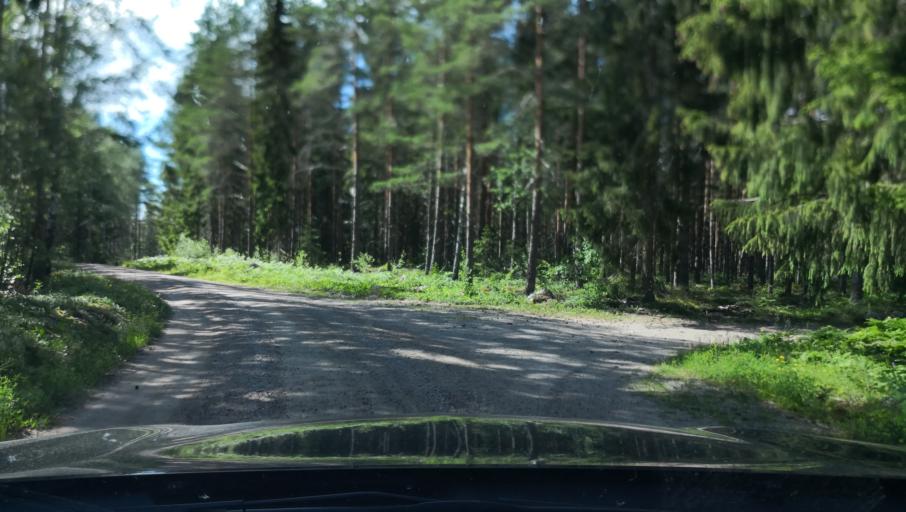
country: SE
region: Vaestmanland
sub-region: Kungsors Kommun
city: Kungsoer
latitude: 59.3264
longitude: 16.0419
